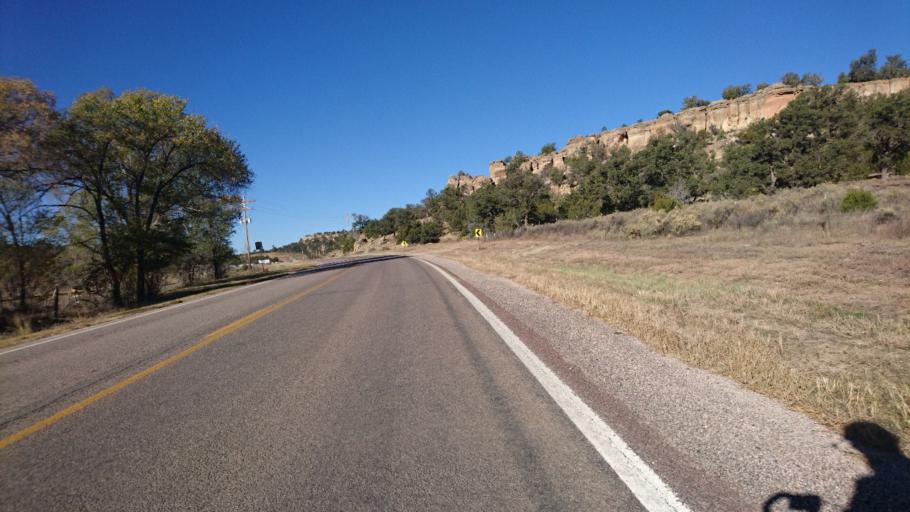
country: US
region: New Mexico
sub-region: McKinley County
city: Black Rock
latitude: 35.1333
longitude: -108.5147
